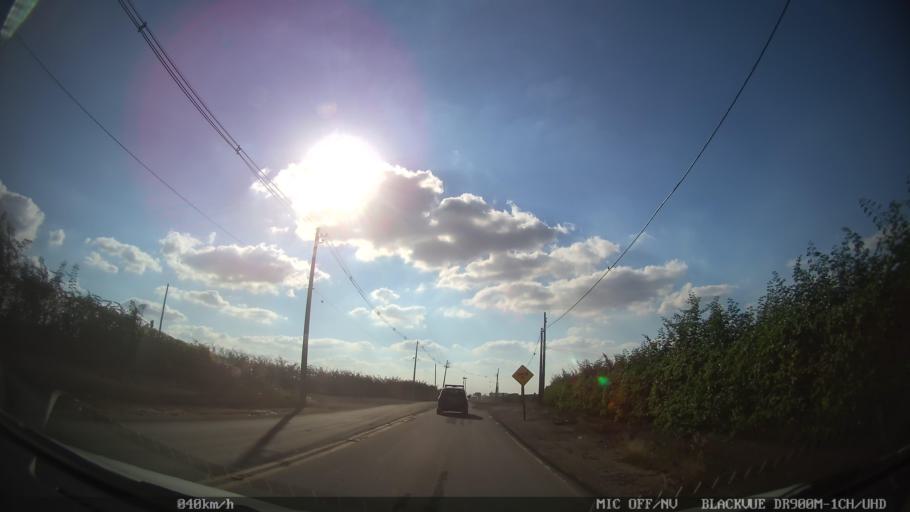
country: BR
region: Sao Paulo
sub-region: Nova Odessa
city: Nova Odessa
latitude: -22.8052
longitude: -47.3334
